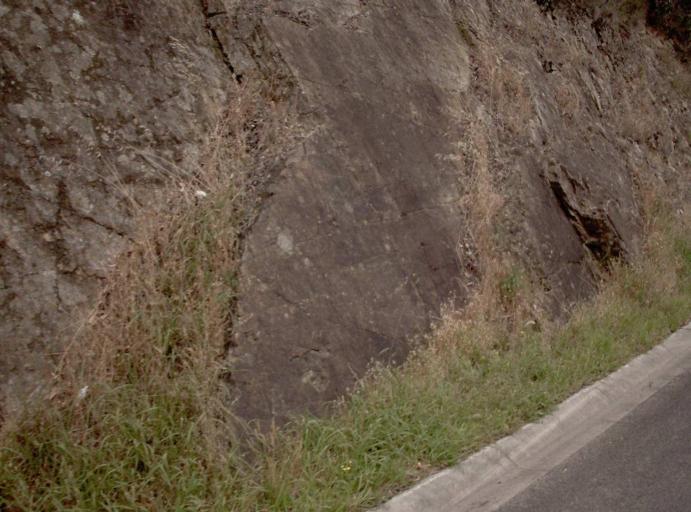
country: AU
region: Victoria
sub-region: Yarra Ranges
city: Yarra Glen
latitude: -37.5719
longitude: 145.4147
